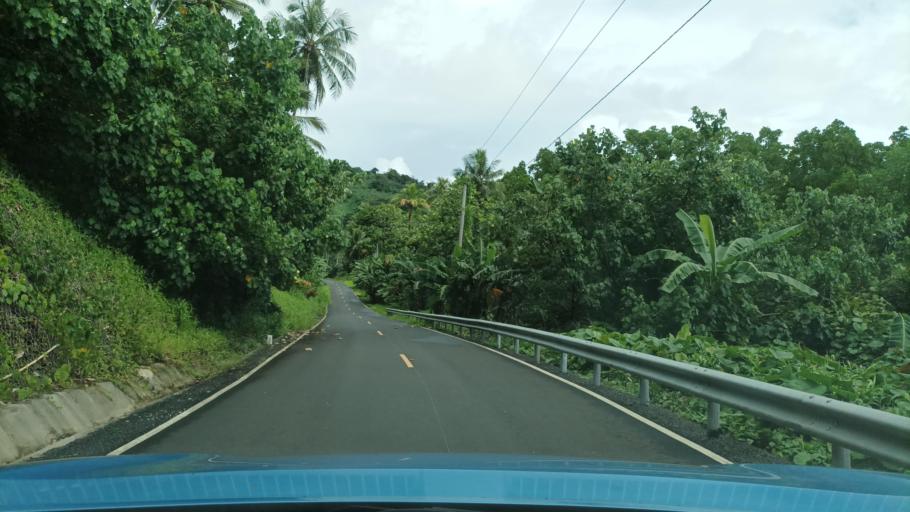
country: FM
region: Pohnpei
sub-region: Madolenihm Municipality
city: Madolenihm Municipality Government
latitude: 6.8664
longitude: 158.3291
